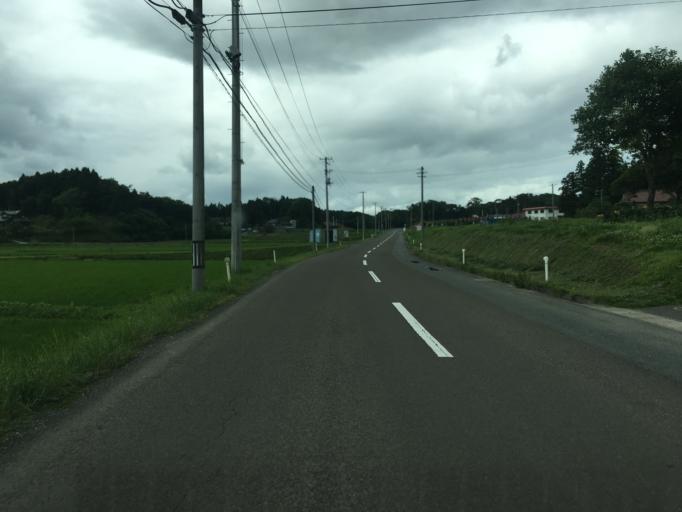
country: JP
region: Miyagi
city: Marumori
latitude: 37.7459
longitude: 140.9653
